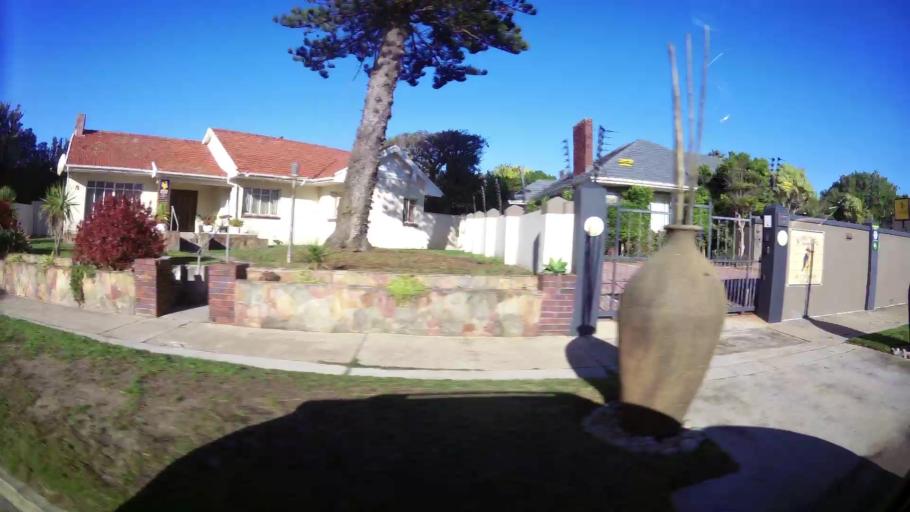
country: ZA
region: Eastern Cape
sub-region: Nelson Mandela Bay Metropolitan Municipality
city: Port Elizabeth
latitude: -33.9912
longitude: 25.6715
